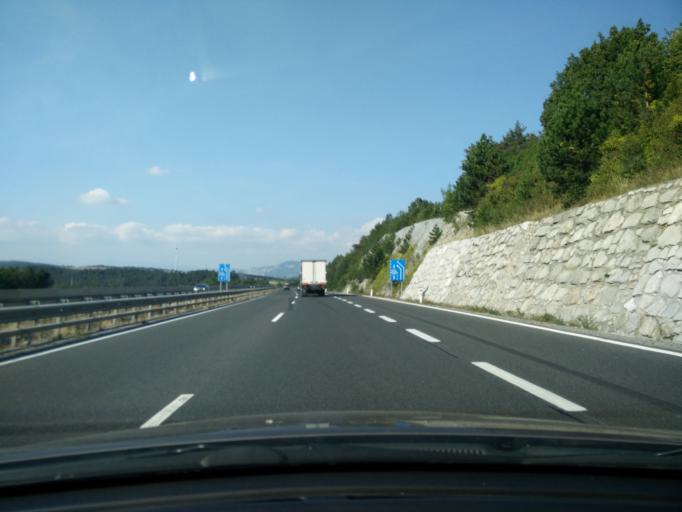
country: SI
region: Divaca
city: Divaca
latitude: 45.7101
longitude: 14.0021
